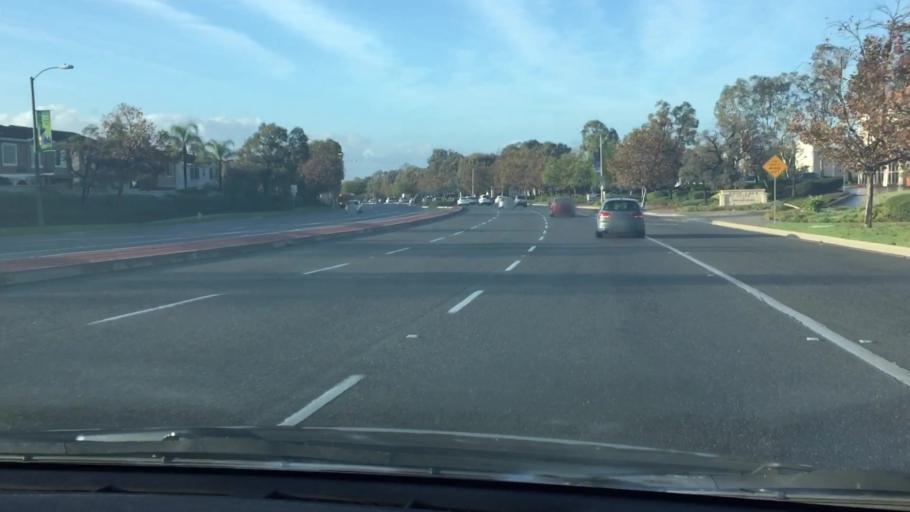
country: US
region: California
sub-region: Orange County
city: Rancho Santa Margarita
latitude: 33.6278
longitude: -117.6047
